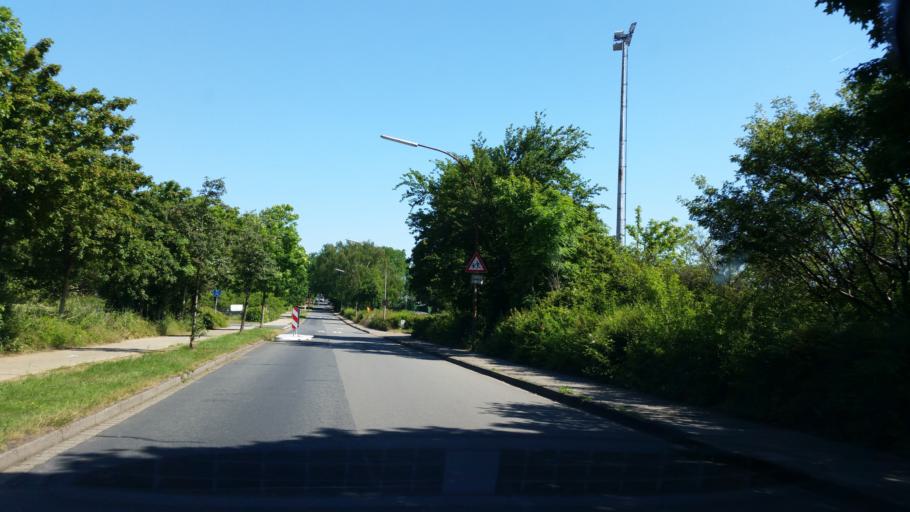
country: DE
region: Lower Saxony
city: Seevetal
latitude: 53.4108
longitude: 10.0245
